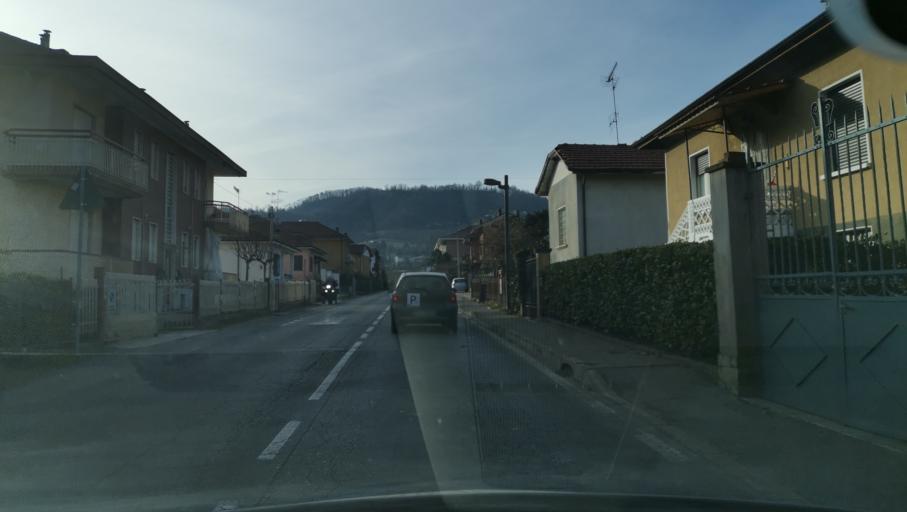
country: IT
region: Piedmont
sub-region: Provincia di Torino
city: Castiglione Torinese
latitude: 45.1101
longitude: 7.8163
